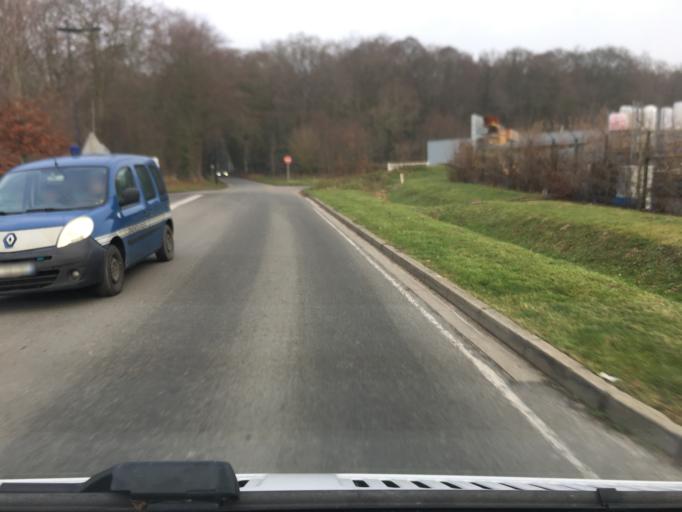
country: FR
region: Picardie
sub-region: Departement de la Somme
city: Saint-Valery-sur-Somme
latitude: 50.1739
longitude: 1.6362
